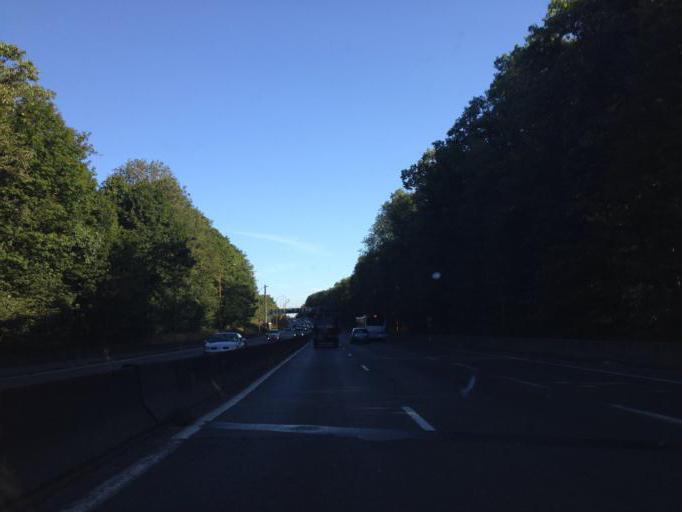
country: FR
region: Ile-de-France
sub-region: Departement des Hauts-de-Seine
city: Meudon
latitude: 48.7979
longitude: 2.2167
